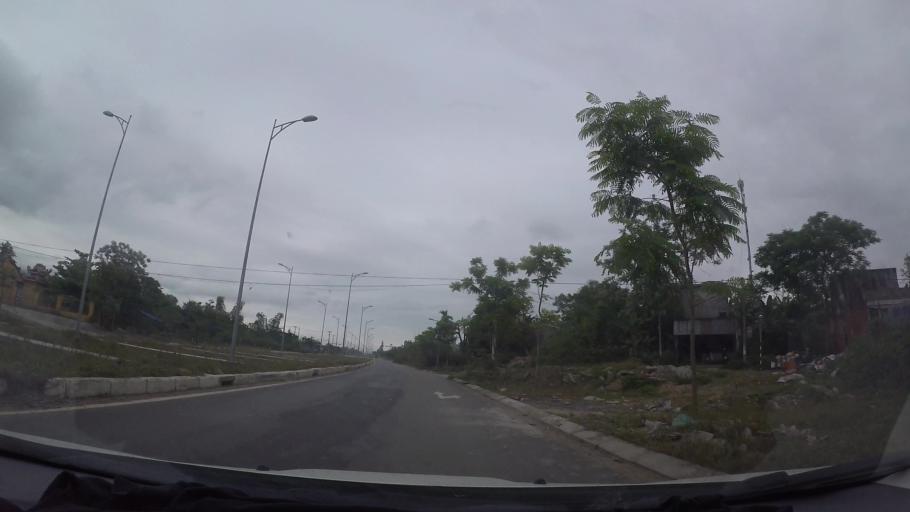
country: VN
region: Da Nang
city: Lien Chieu
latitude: 16.0785
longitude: 108.0967
